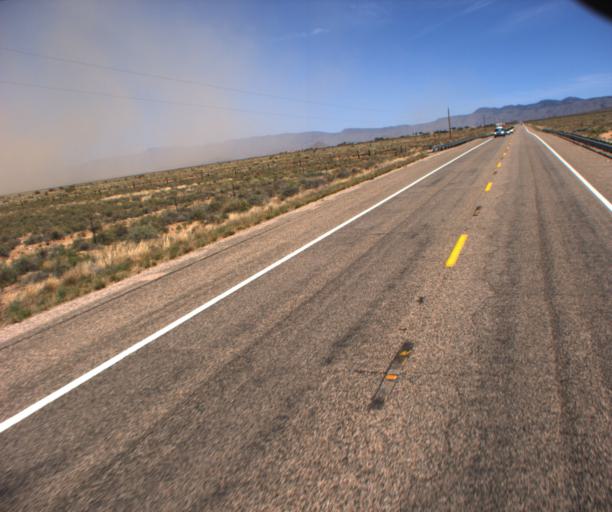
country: US
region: Arizona
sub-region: Mohave County
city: New Kingman-Butler
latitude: 35.3668
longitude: -113.8675
